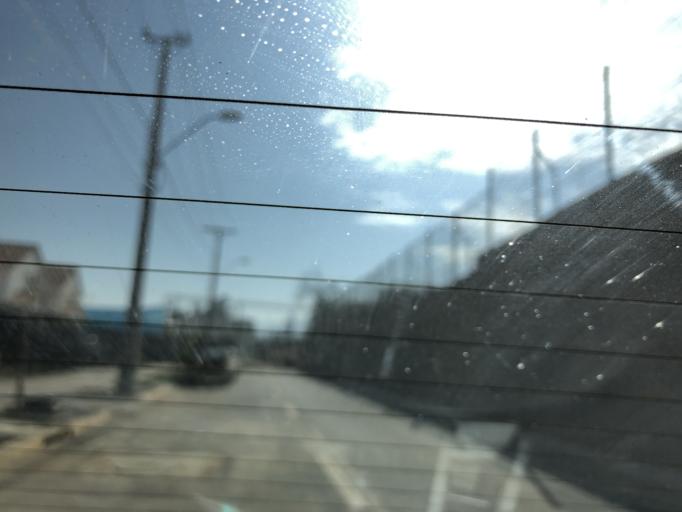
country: CL
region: Santiago Metropolitan
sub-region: Provincia de Cordillera
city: Puente Alto
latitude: -33.5708
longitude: -70.5400
